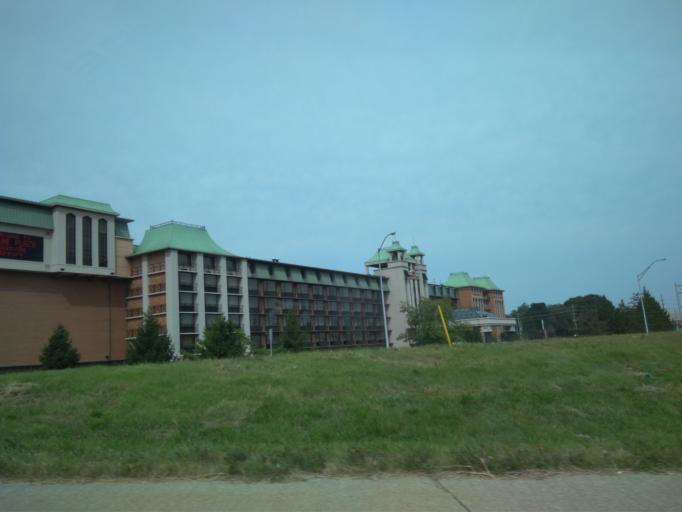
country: US
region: Kentucky
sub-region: Jefferson County
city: Audubon Park
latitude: 38.1913
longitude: -85.7390
